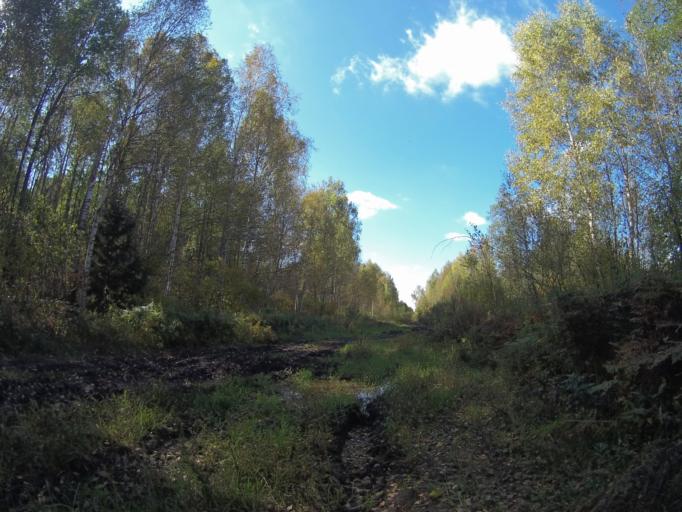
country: RU
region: Vladimir
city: Raduzhnyy
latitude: 55.9401
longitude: 40.2391
